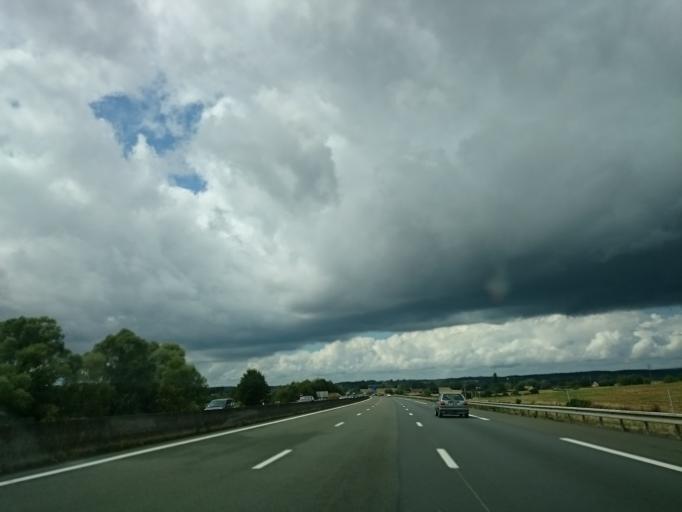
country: FR
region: Pays de la Loire
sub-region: Departement de la Sarthe
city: Sarge-les-le-Mans
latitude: 48.0589
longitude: 0.2291
